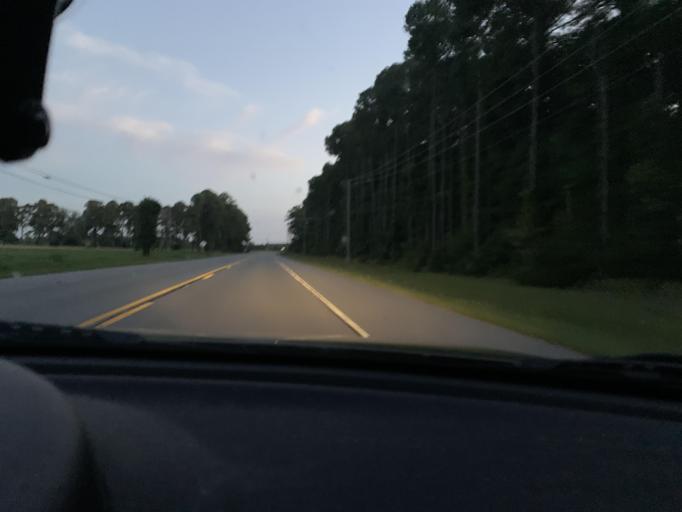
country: US
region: Maryland
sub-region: Talbot County
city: Saint Michaels
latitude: 38.7556
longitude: -76.3198
